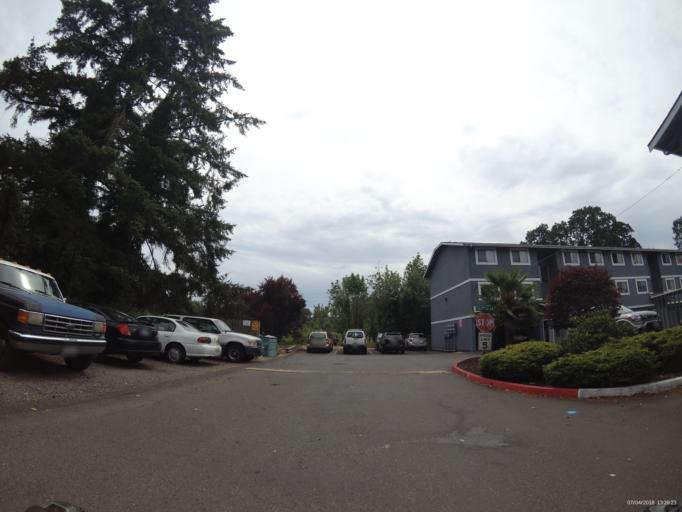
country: US
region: Washington
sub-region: Pierce County
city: McChord Air Force Base
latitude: 47.1472
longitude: -122.5006
